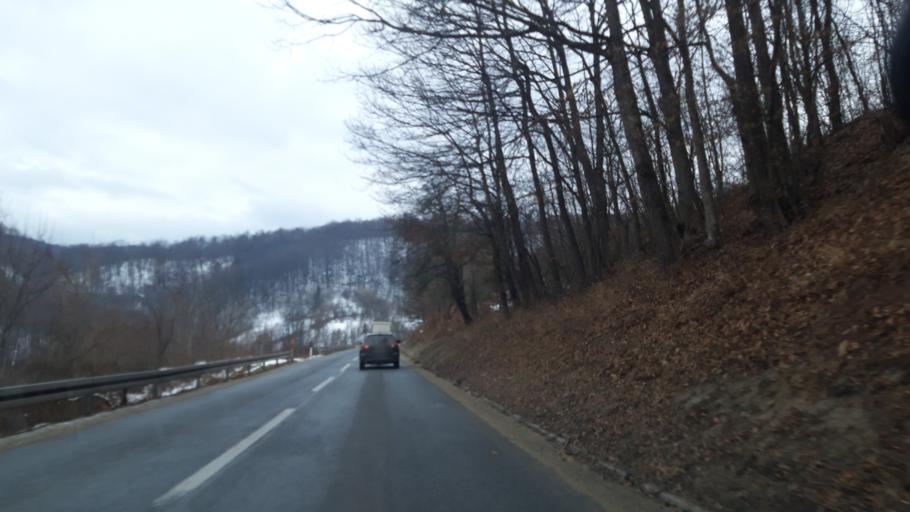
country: BA
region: Republika Srpska
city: Vlasenica
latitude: 44.1810
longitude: 18.9817
